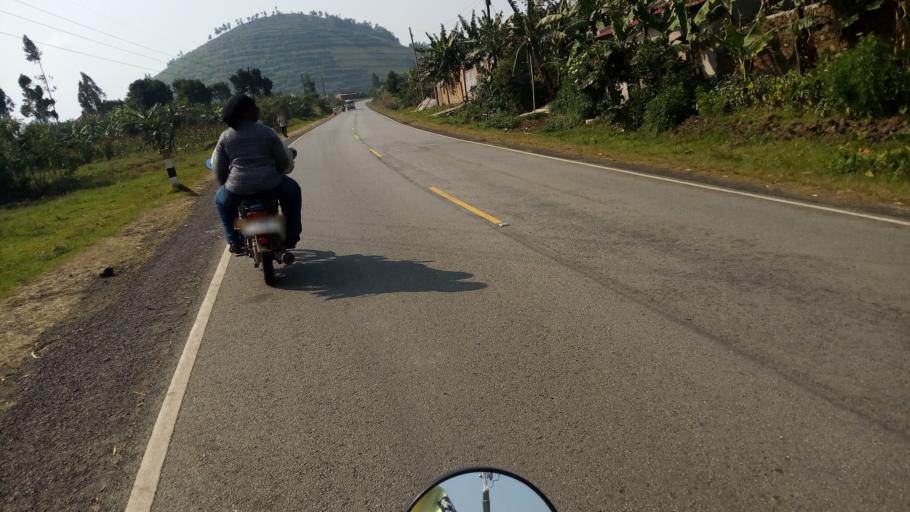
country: UG
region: Western Region
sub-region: Kisoro District
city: Kisoro
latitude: -1.2940
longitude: 29.7184
